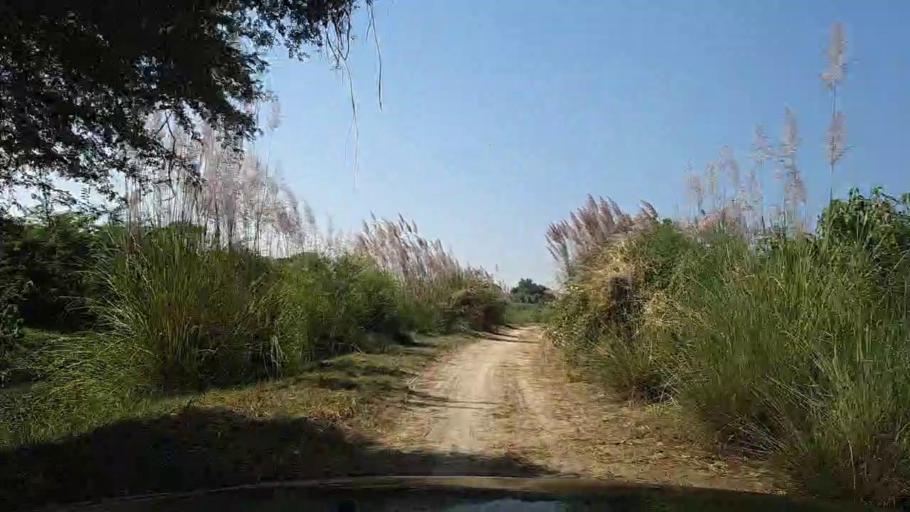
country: PK
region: Sindh
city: Mirpur Sakro
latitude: 24.5749
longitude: 67.7906
